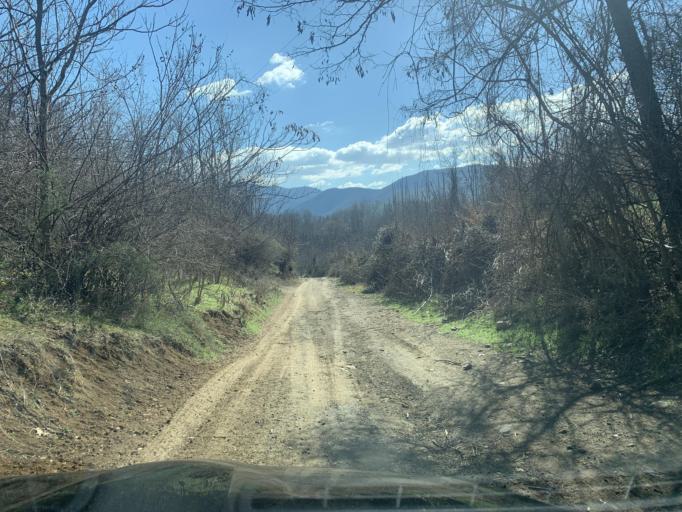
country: MK
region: Demir Kapija
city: Demir Kapija
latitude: 41.3981
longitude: 22.2181
